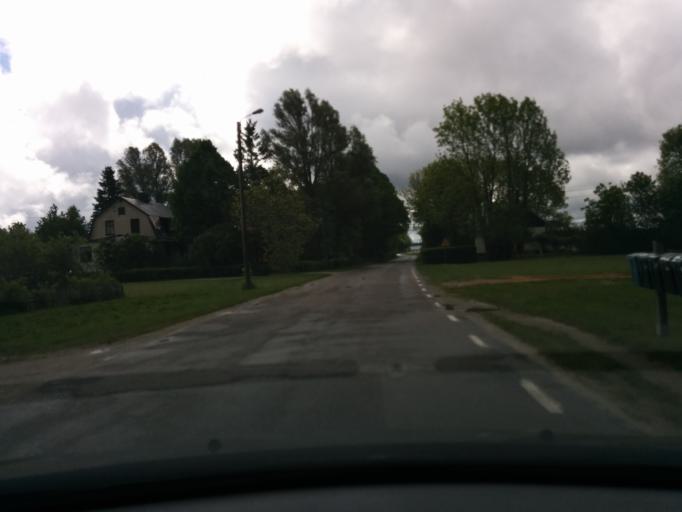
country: SE
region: Gotland
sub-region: Gotland
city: Slite
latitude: 57.5777
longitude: 18.7310
